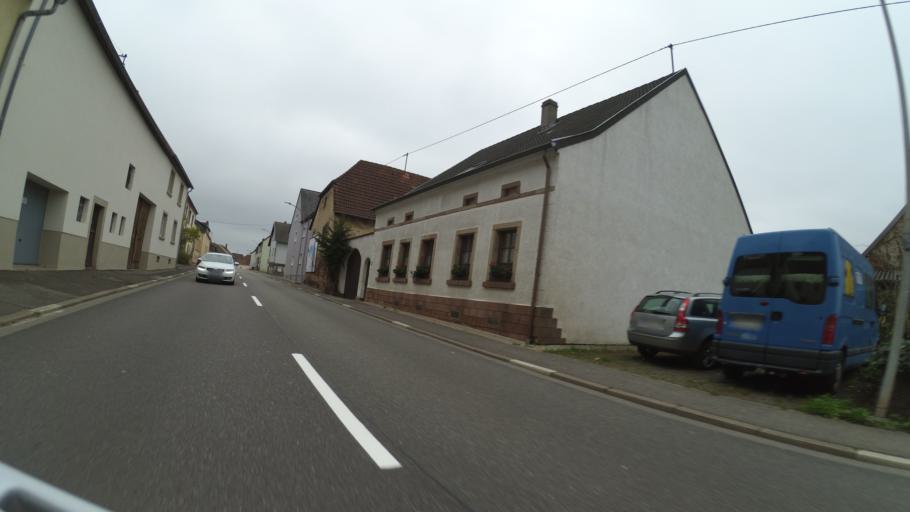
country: DE
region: Saarland
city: Blieskastel
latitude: 49.2435
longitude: 7.2734
